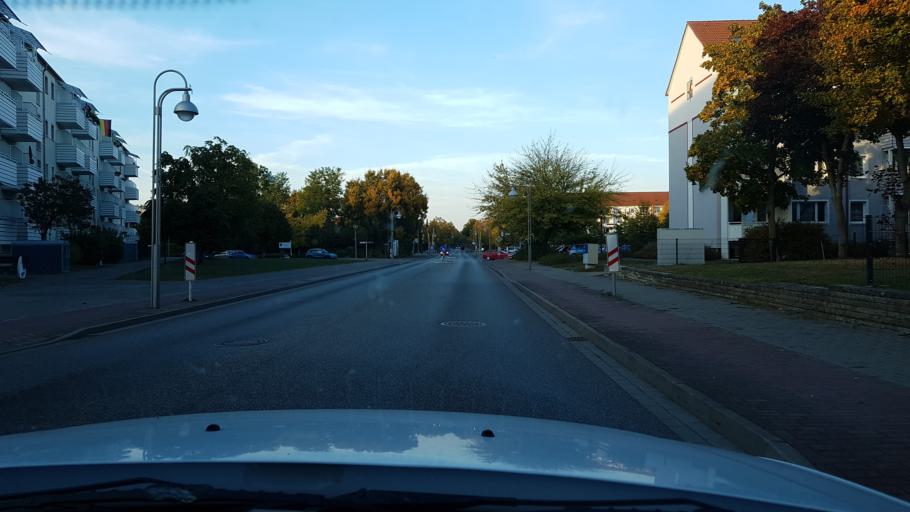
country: DE
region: Brandenburg
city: Schwedt (Oder)
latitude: 53.0601
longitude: 14.2948
